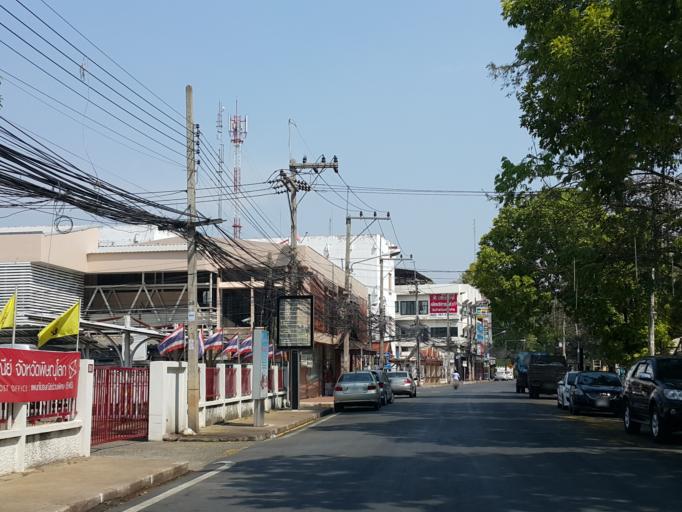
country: TH
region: Phitsanulok
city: Phitsanulok
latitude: 16.8177
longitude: 100.2601
